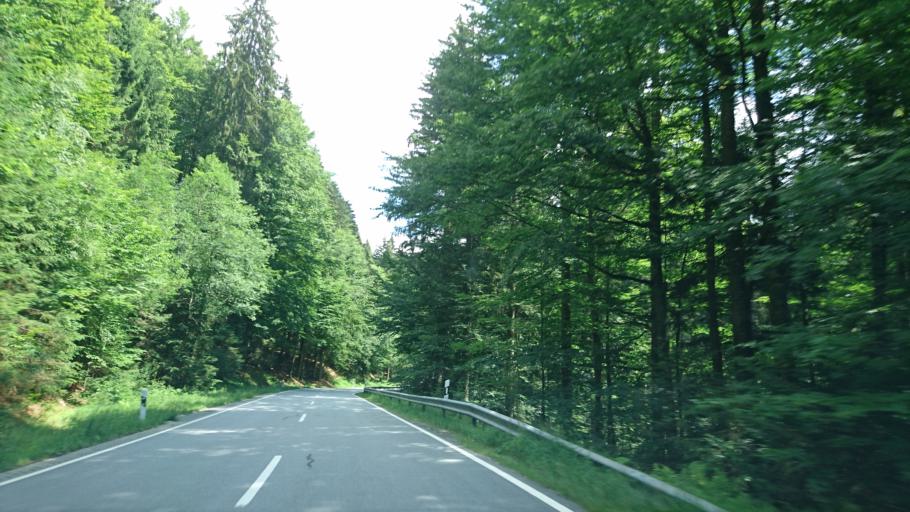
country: DE
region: Bavaria
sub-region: Lower Bavaria
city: Mauth
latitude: 48.8759
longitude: 13.5732
